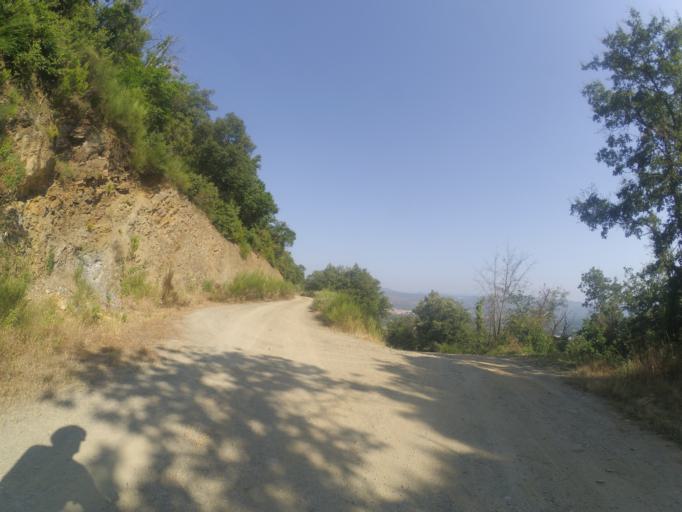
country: FR
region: Languedoc-Roussillon
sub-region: Departement des Pyrenees-Orientales
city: Ille-sur-Tet
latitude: 42.6472
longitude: 2.6398
